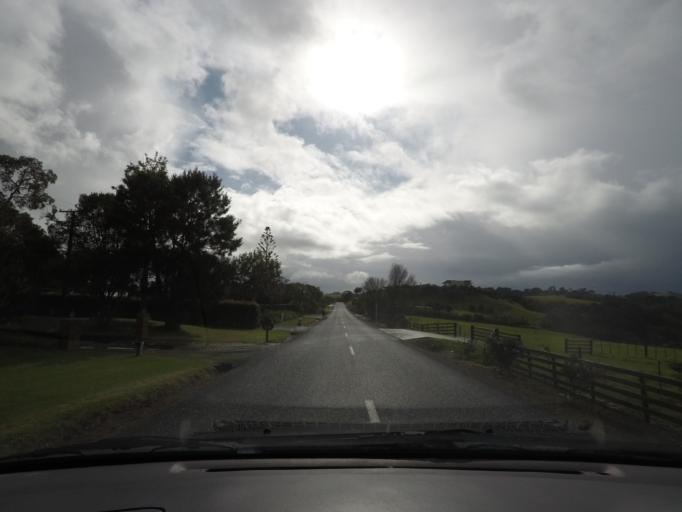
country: NZ
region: Auckland
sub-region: Auckland
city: Warkworth
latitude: -36.4712
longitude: 174.7346
